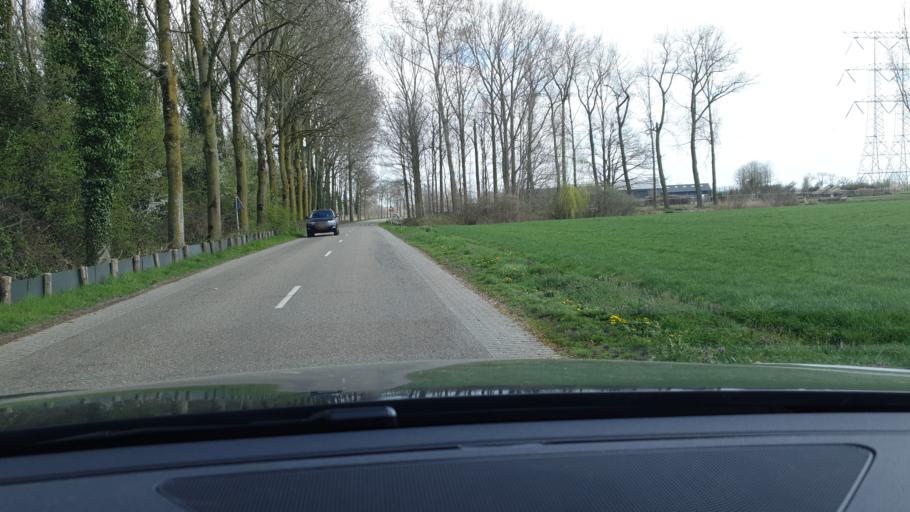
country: NL
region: North Brabant
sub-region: Gemeente Oirschot
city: Oirschot
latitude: 51.5244
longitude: 5.3425
